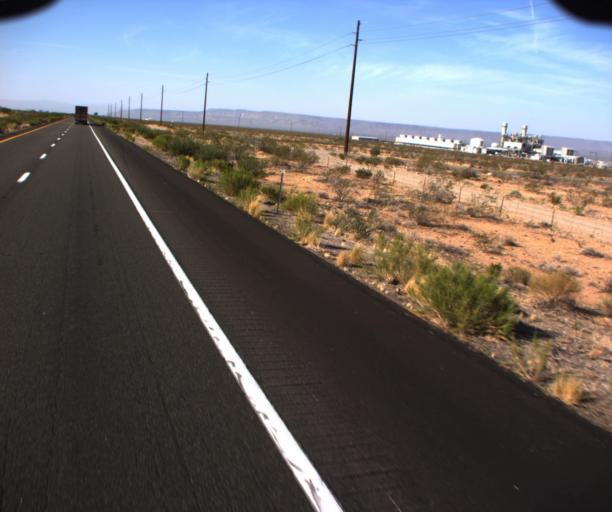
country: US
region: Arizona
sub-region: Mohave County
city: Kingman
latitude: 35.0593
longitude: -114.1260
